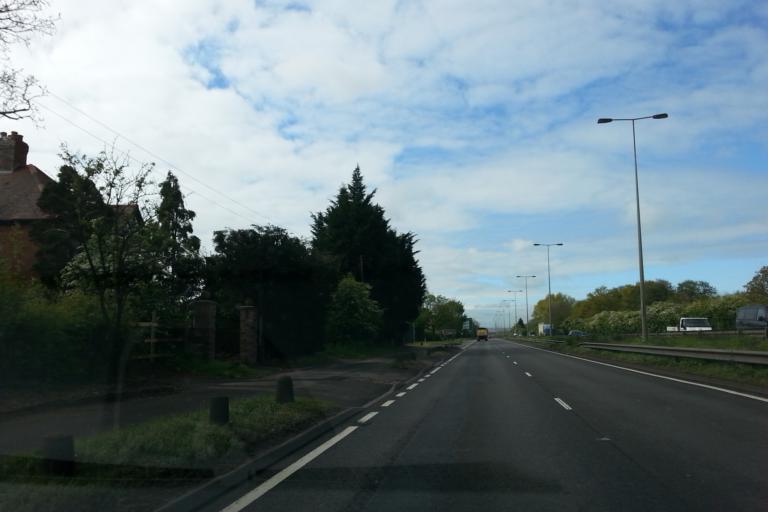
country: GB
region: England
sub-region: Staffordshire
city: Barton under Needwood
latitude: 52.7694
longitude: -1.6919
